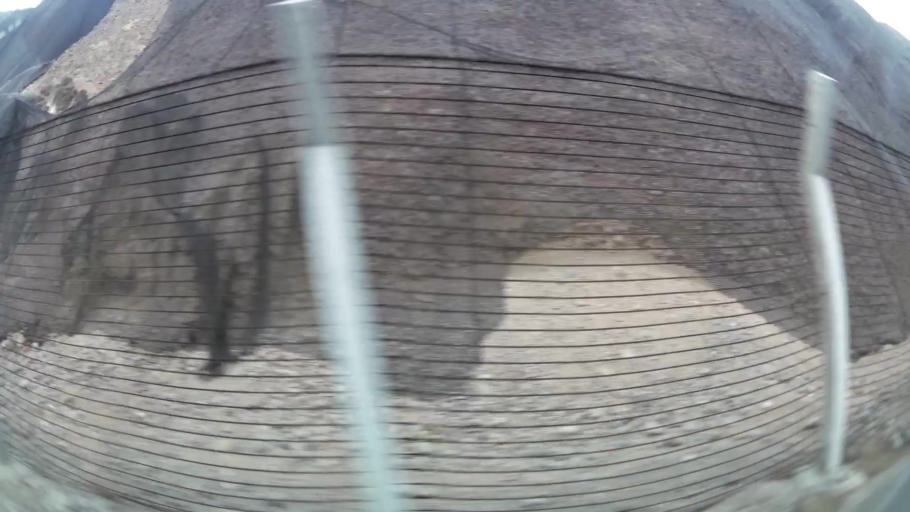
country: PE
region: Lima
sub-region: Lima
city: San Isidro
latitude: -12.1257
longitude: -77.0385
